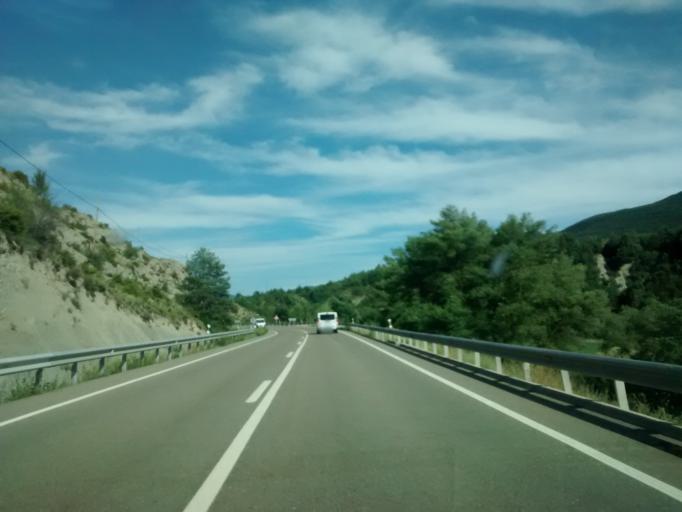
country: ES
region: Aragon
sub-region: Provincia de Huesca
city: Yebra de Basa
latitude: 42.4902
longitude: -0.3172
